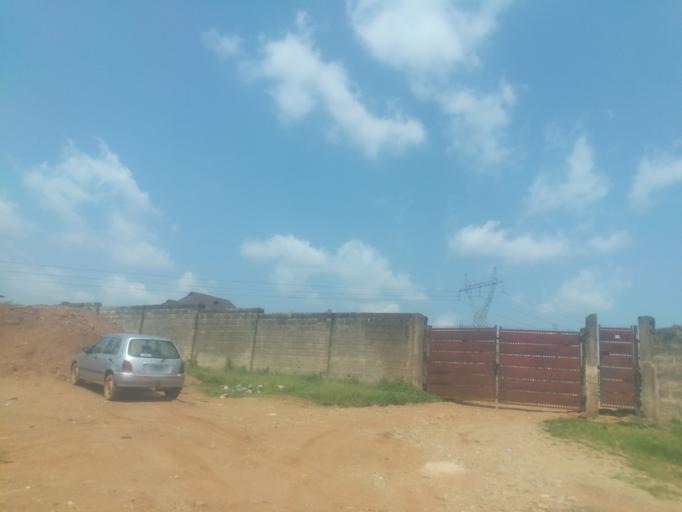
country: NG
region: Oyo
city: Moniya
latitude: 7.5185
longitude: 3.9140
